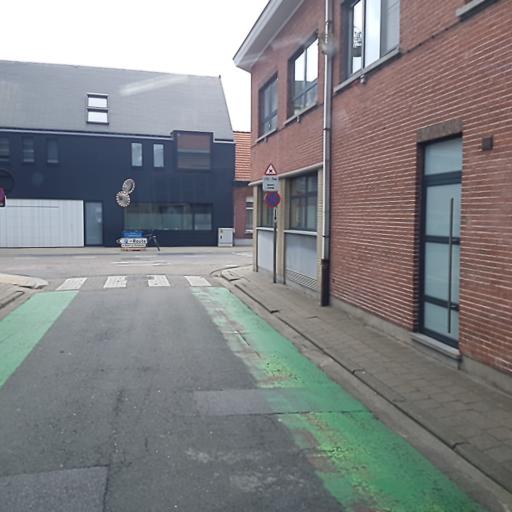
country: BE
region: Flanders
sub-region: Provincie Antwerpen
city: Kapellen
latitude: 51.3113
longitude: 4.4221
